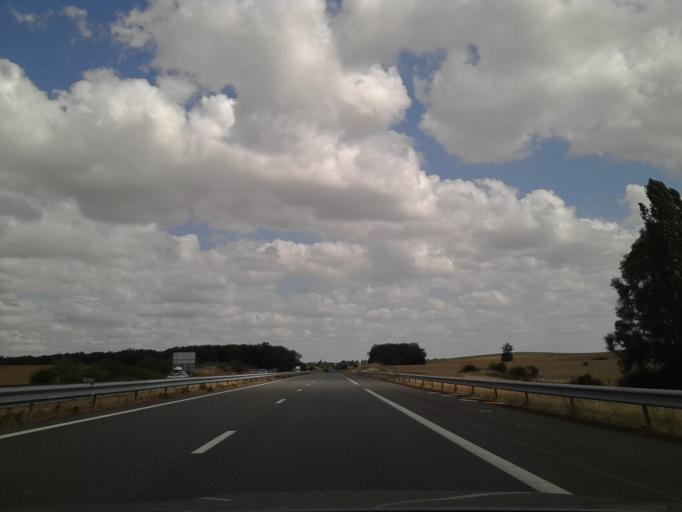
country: FR
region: Centre
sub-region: Departement du Cher
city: Orval
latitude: 46.6711
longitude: 2.4666
